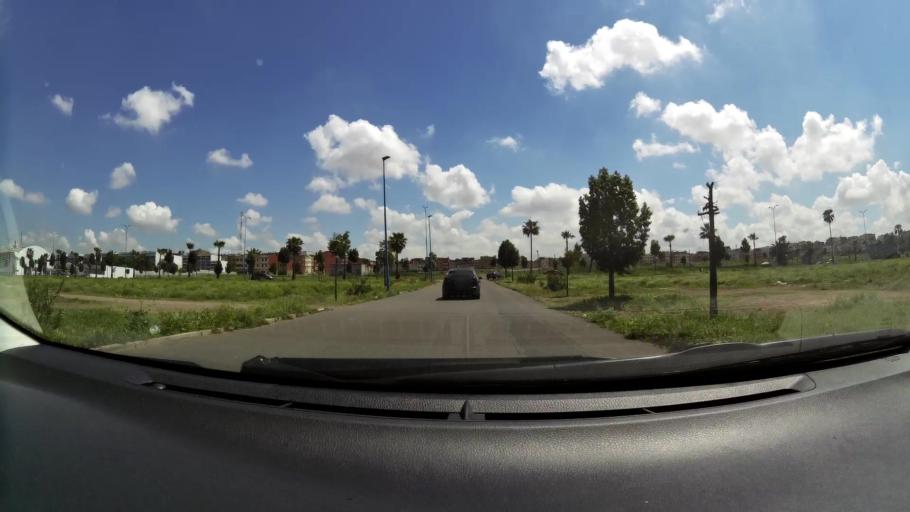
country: MA
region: Grand Casablanca
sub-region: Casablanca
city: Casablanca
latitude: 33.5592
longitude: -7.5783
